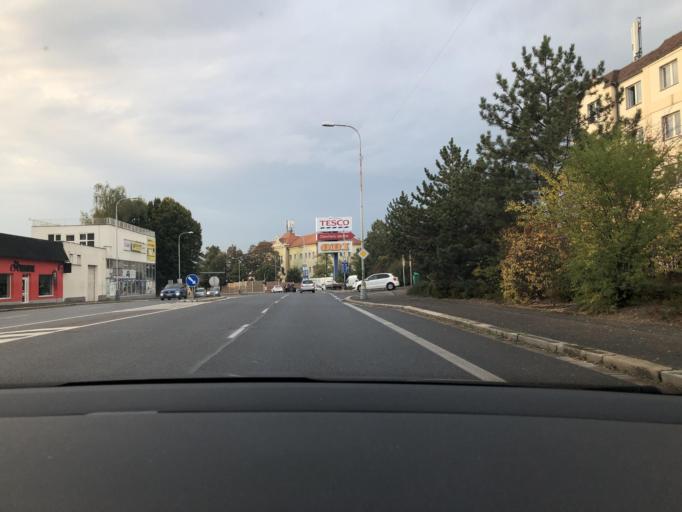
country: CZ
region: Central Bohemia
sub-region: Okres Kolin
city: Kolin
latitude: 50.0298
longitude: 15.1905
